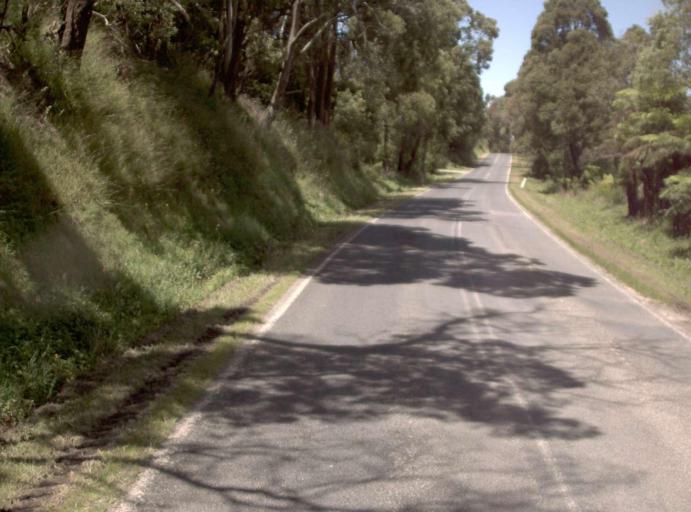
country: AU
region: Victoria
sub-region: Bass Coast
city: North Wonthaggi
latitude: -38.7210
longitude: 146.1206
